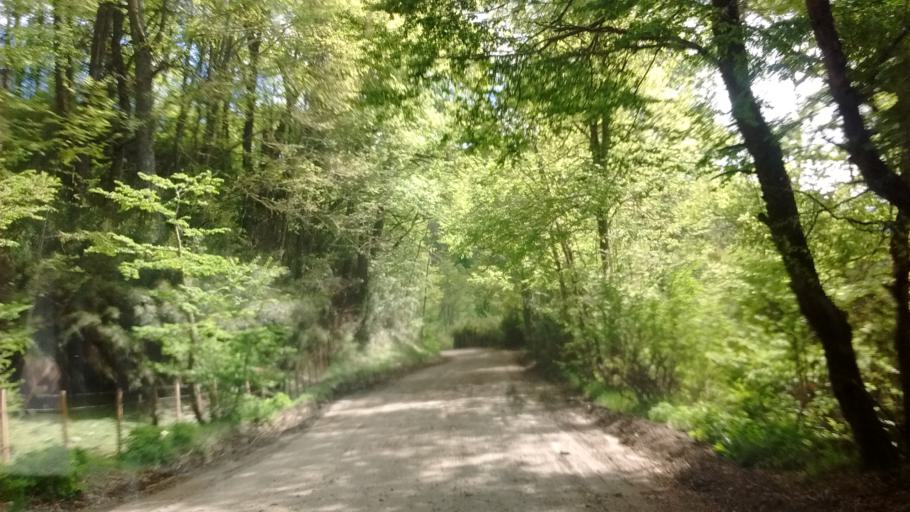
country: AR
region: Neuquen
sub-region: Departamento de Lacar
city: San Martin de los Andes
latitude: -40.3630
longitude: -71.4760
